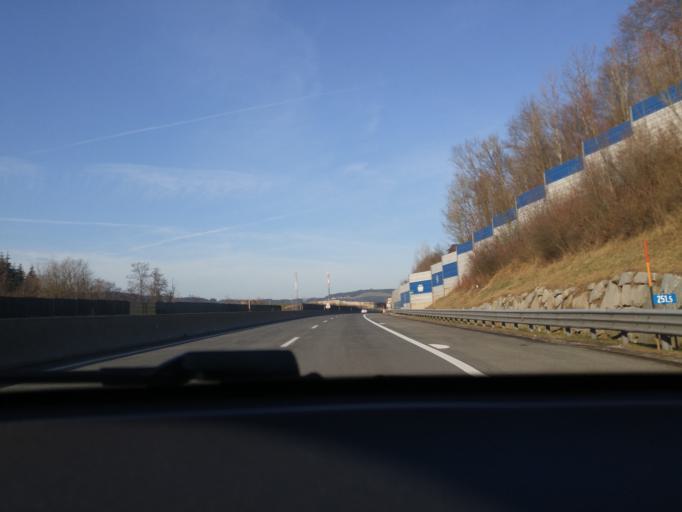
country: AT
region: Upper Austria
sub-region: Politischer Bezirk Vocklabruck
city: Oberwang
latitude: 47.8791
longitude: 13.4334
